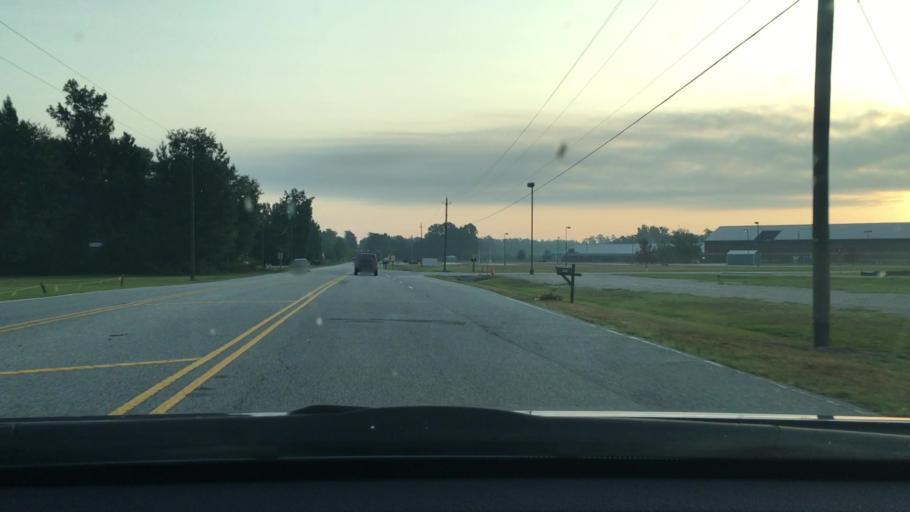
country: US
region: South Carolina
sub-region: Darlington County
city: Hartsville
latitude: 34.3401
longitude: -80.1001
